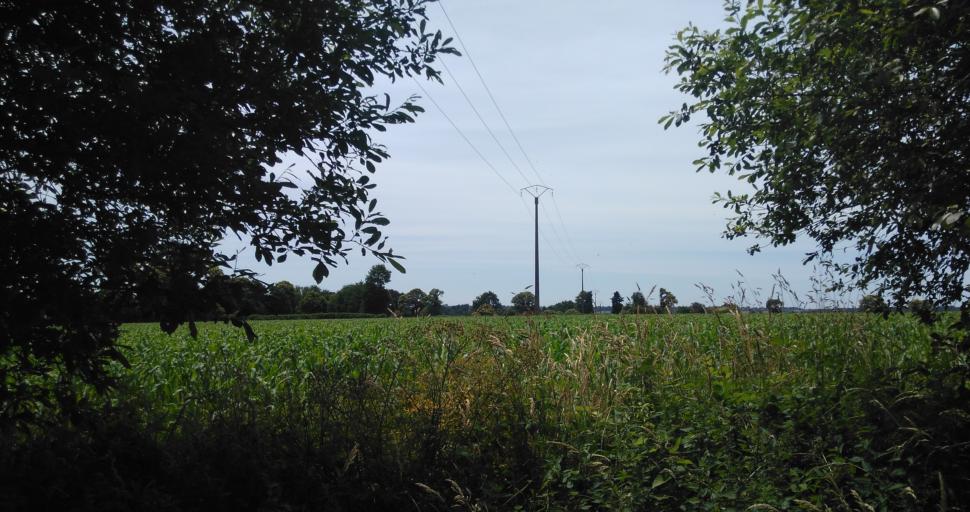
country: FR
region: Brittany
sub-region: Departement d'Ille-et-Vilaine
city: La Meziere
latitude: 48.2185
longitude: -1.7656
